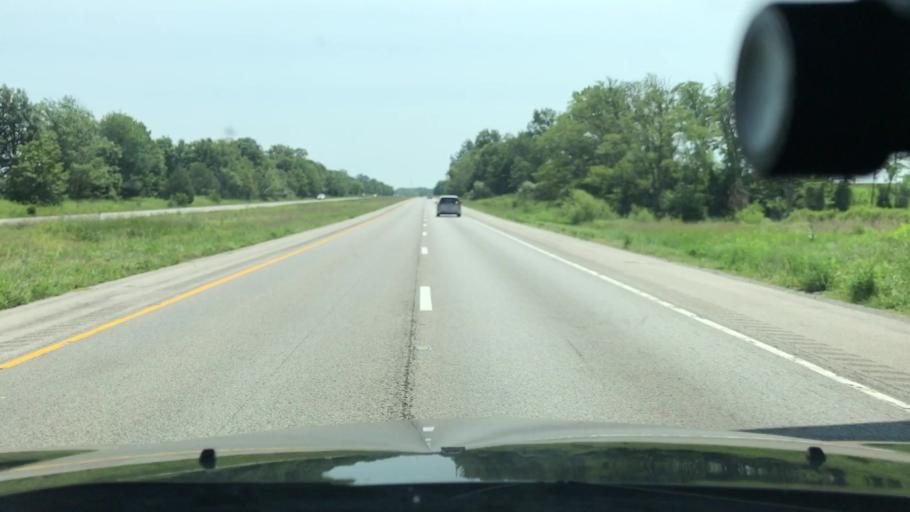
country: US
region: Illinois
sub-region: Jefferson County
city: Mount Vernon
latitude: 38.3534
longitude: -88.9923
